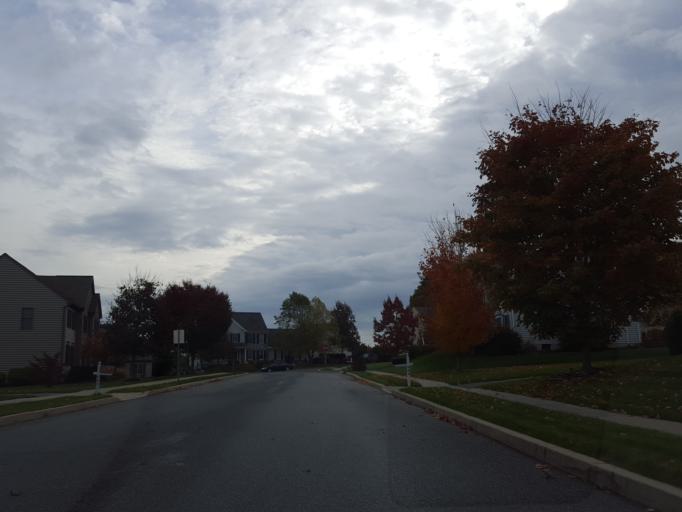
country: US
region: Pennsylvania
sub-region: York County
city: Spry
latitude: 39.9281
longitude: -76.6645
